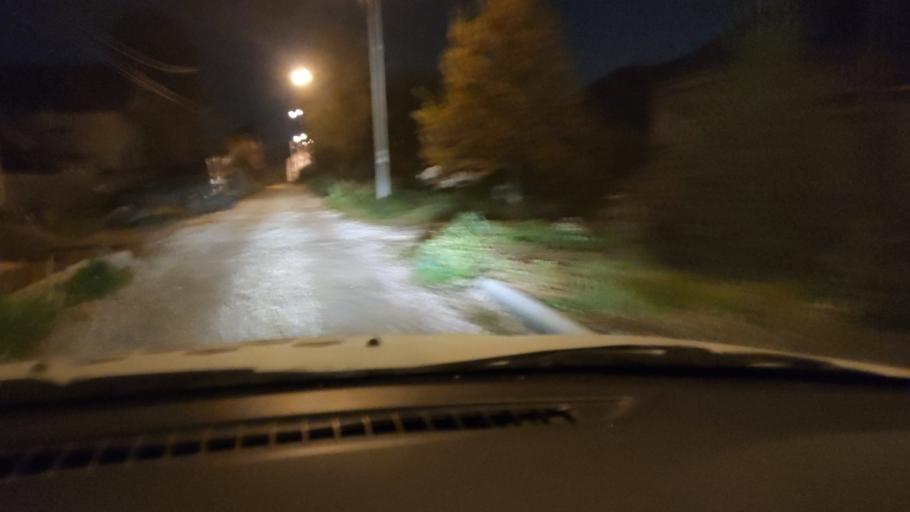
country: RU
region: Perm
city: Perm
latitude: 57.9754
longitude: 56.2980
